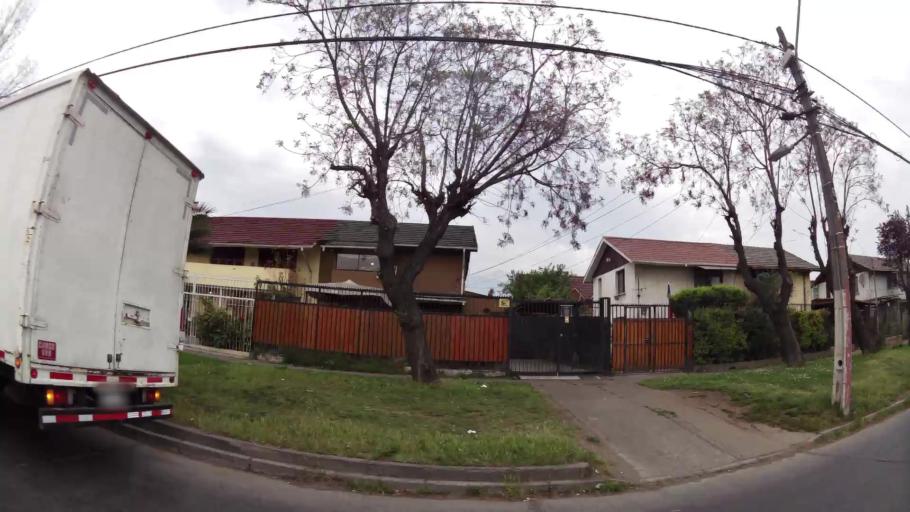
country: CL
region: Santiago Metropolitan
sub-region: Provincia de Santiago
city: Villa Presidente Frei, Nunoa, Santiago, Chile
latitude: -33.4754
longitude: -70.6134
